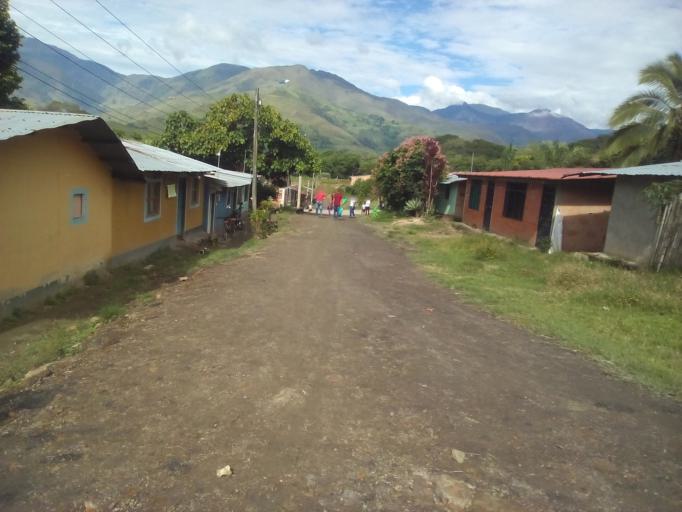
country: CO
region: Casanare
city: Nunchia
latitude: 5.6266
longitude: -72.4227
